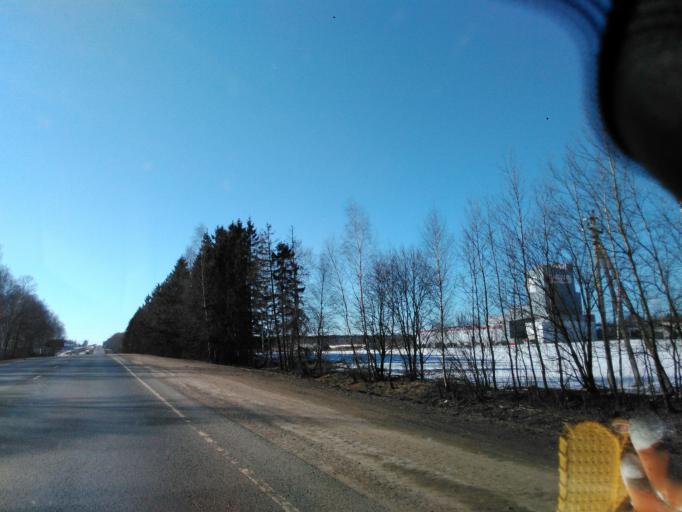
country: RU
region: Moskovskaya
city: Yermolino
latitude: 56.1361
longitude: 37.4316
